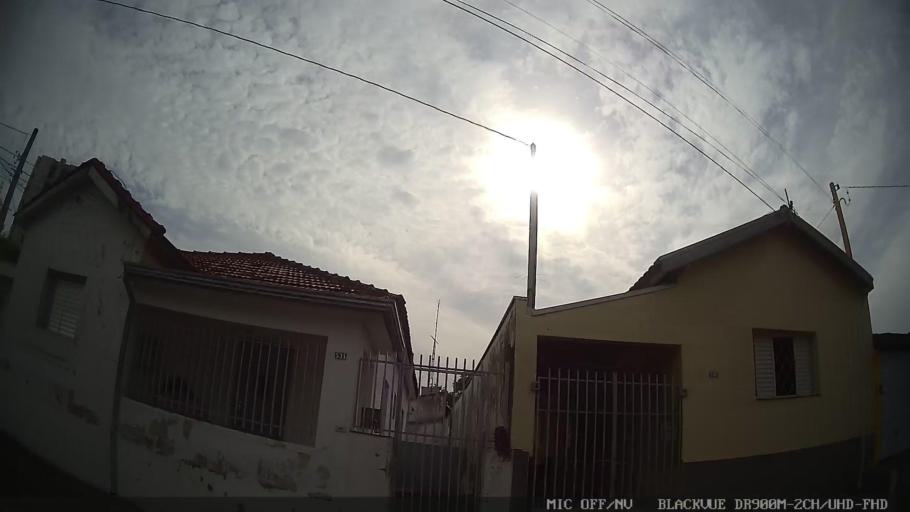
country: BR
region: Sao Paulo
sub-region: Indaiatuba
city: Indaiatuba
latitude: -23.0850
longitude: -47.2195
